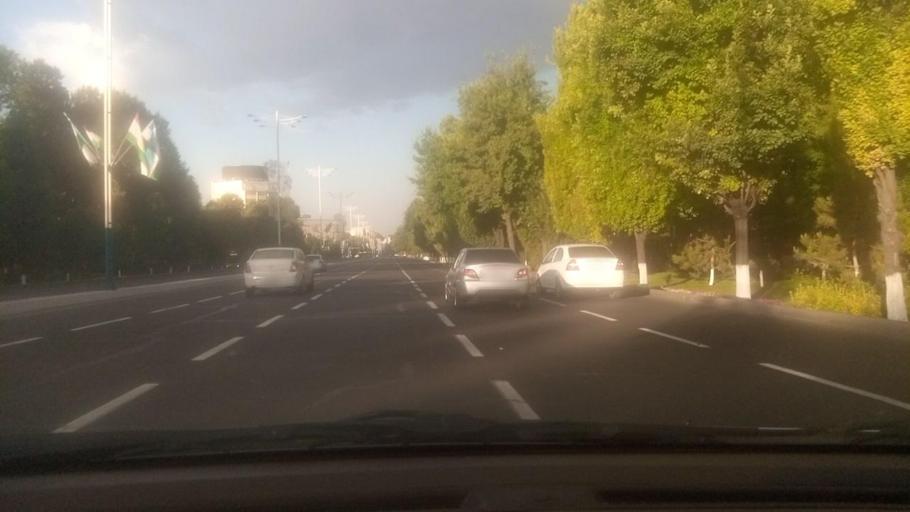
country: UZ
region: Toshkent
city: Salor
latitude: 41.3292
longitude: 69.3293
